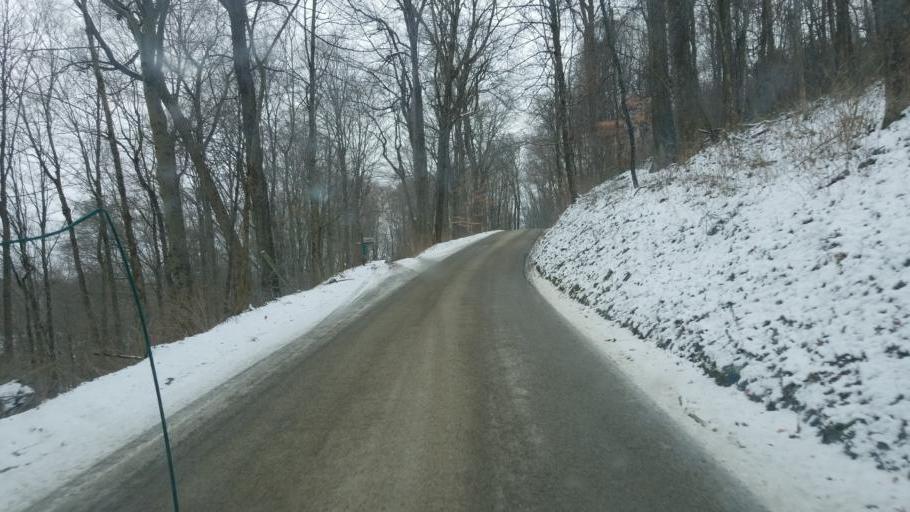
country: US
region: Ohio
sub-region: Sandusky County
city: Bellville
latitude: 40.6108
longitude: -82.4970
